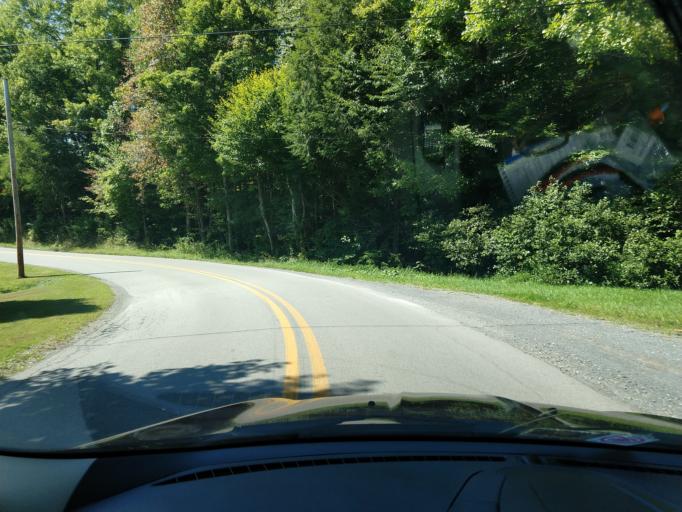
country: US
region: West Virginia
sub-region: Nicholas County
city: Summersville
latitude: 38.2776
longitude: -80.7664
